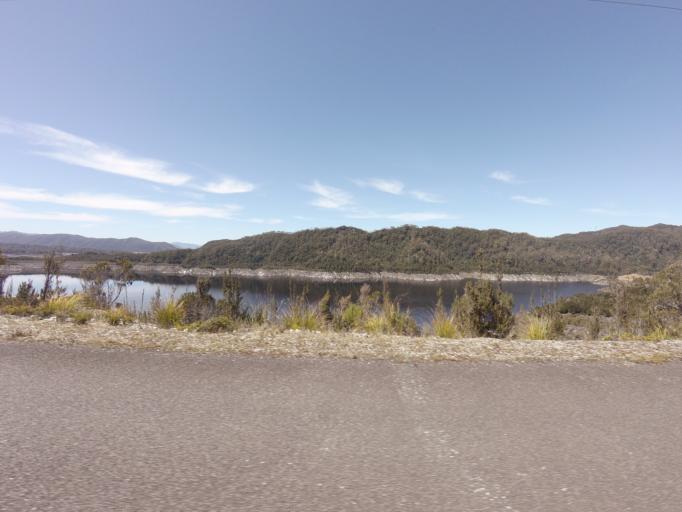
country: AU
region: Tasmania
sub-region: West Coast
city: Queenstown
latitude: -42.7416
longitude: 145.9809
